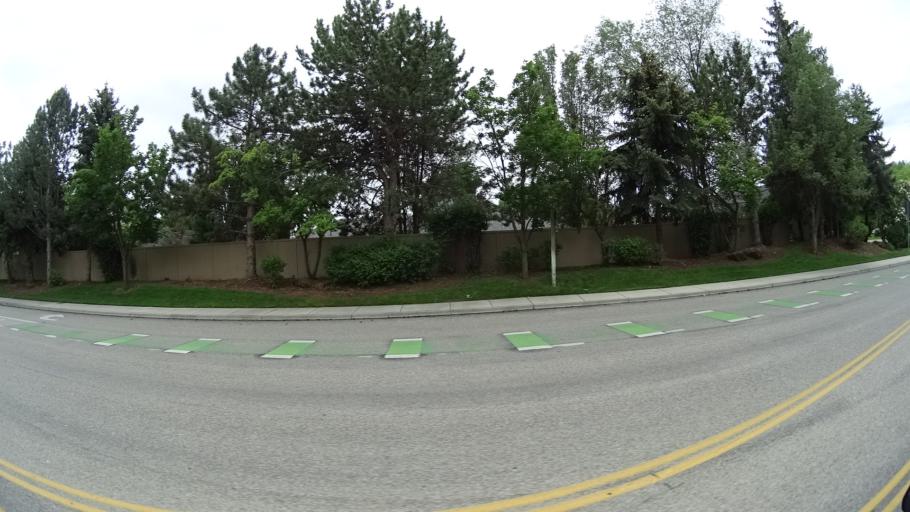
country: US
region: Idaho
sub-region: Ada County
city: Eagle
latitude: 43.7065
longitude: -116.3200
